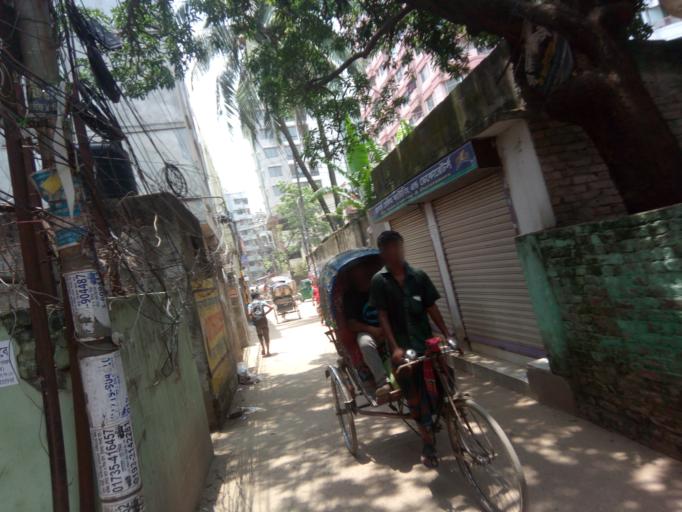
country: BD
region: Dhaka
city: Paltan
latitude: 23.7401
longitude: 90.4151
